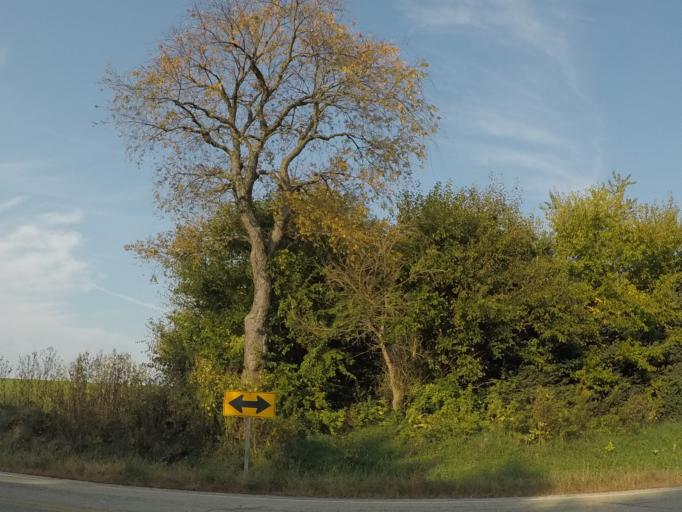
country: US
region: Wisconsin
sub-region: Dane County
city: Cross Plains
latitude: 43.0422
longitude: -89.6161
